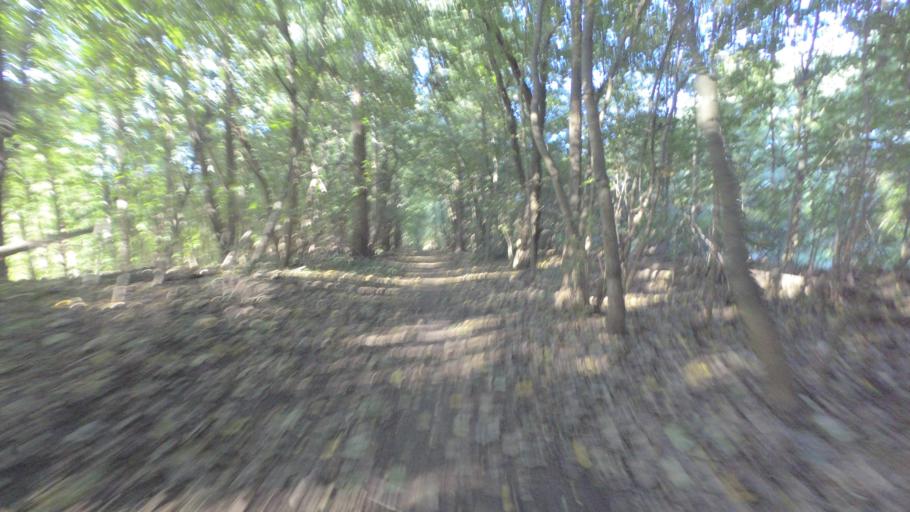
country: DE
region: Brandenburg
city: Rangsdorf
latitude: 52.3331
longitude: 13.4170
